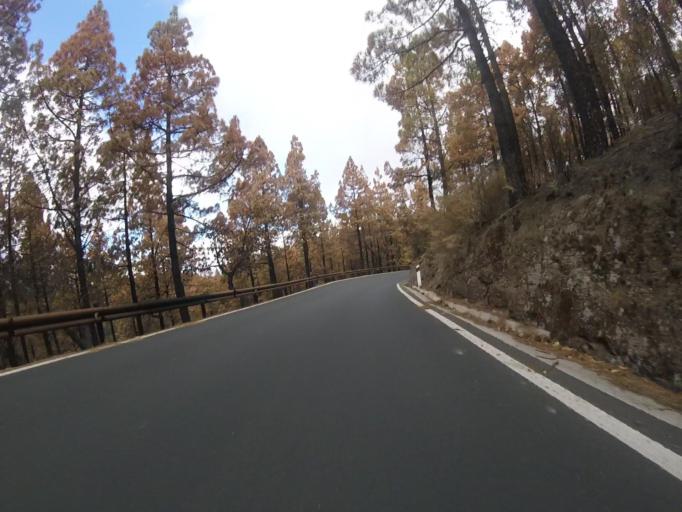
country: ES
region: Canary Islands
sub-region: Provincia de Las Palmas
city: Tejeda
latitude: 27.9752
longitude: -15.5785
